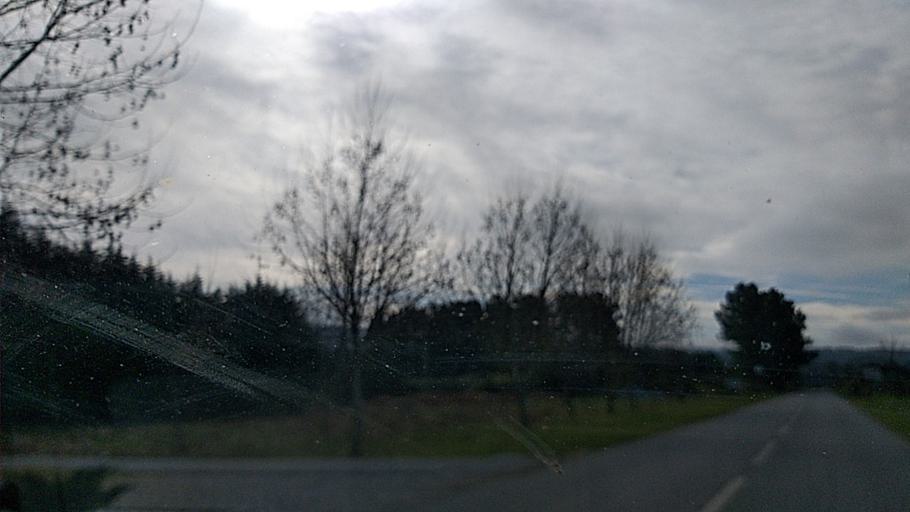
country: PT
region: Guarda
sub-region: Fornos de Algodres
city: Fornos de Algodres
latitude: 40.6746
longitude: -7.5292
